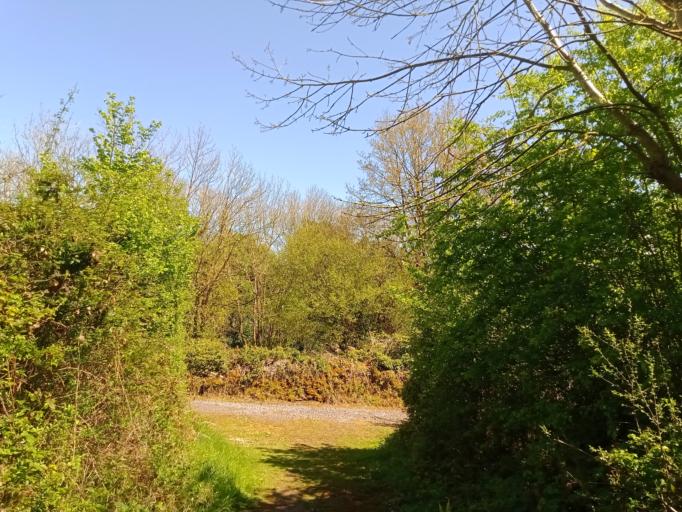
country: IE
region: Leinster
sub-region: Kilkenny
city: Kilkenny
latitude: 52.6913
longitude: -7.2626
